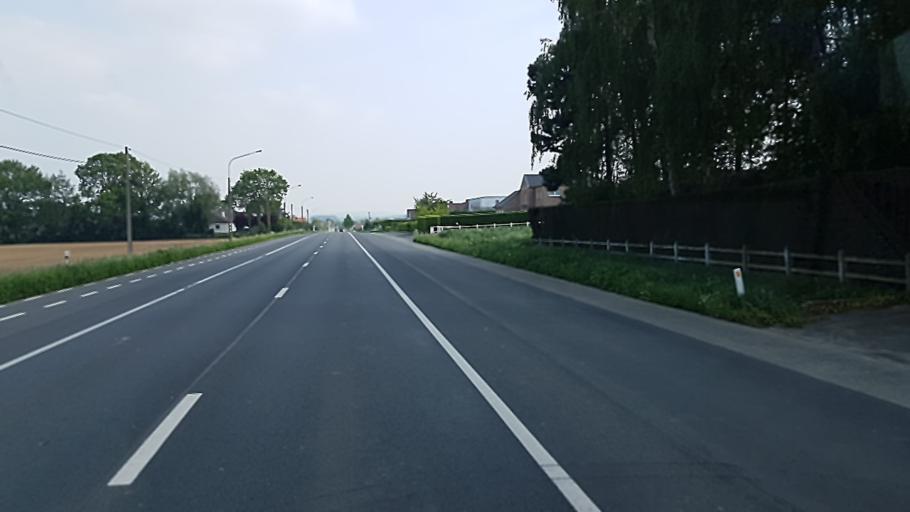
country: BE
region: Wallonia
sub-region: Province du Hainaut
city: Pecq
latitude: 50.7449
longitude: 3.3221
